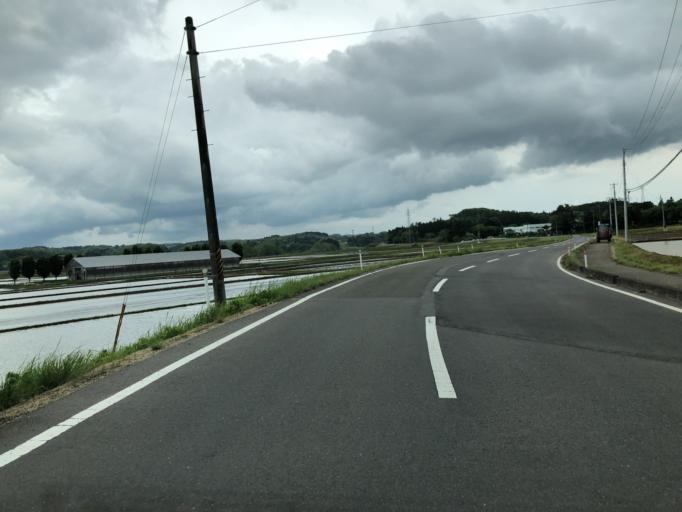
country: JP
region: Fukushima
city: Ishikawa
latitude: 37.1884
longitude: 140.3953
